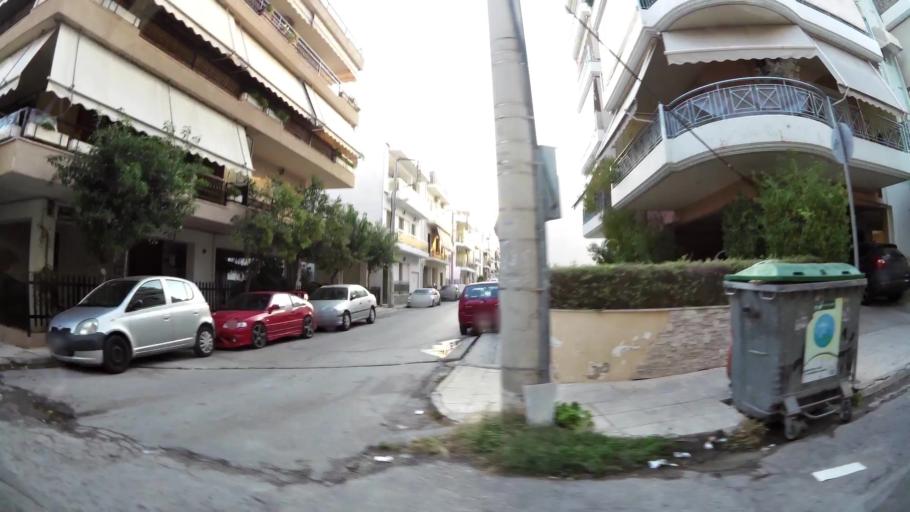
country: GR
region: Attica
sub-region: Nomarchia Athinas
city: Ilion
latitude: 38.0338
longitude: 23.6926
